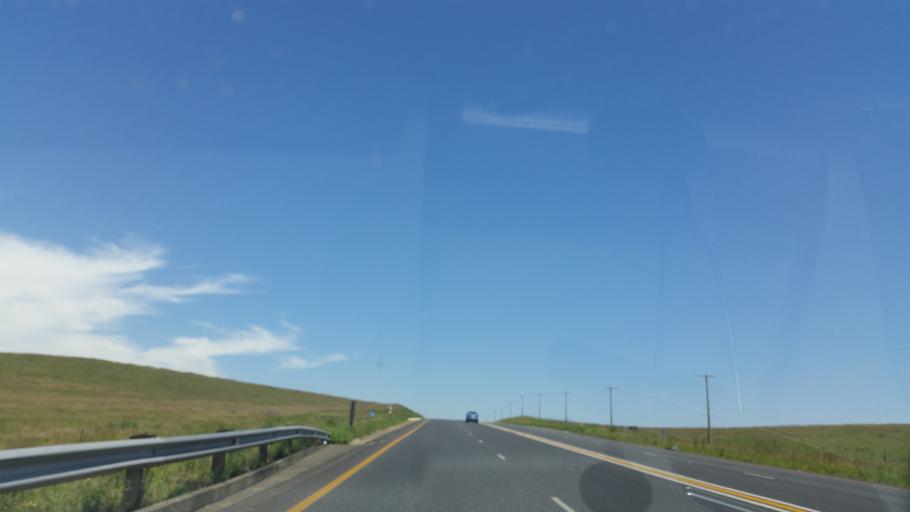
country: ZA
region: Orange Free State
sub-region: Thabo Mofutsanyana District Municipality
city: Harrismith
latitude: -28.3665
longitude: 29.3504
